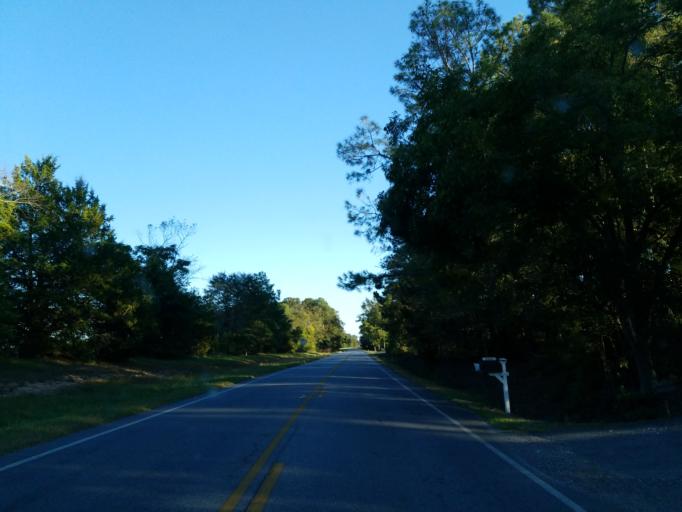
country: US
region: Georgia
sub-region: Worth County
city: Sylvester
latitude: 31.5626
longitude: -83.8505
